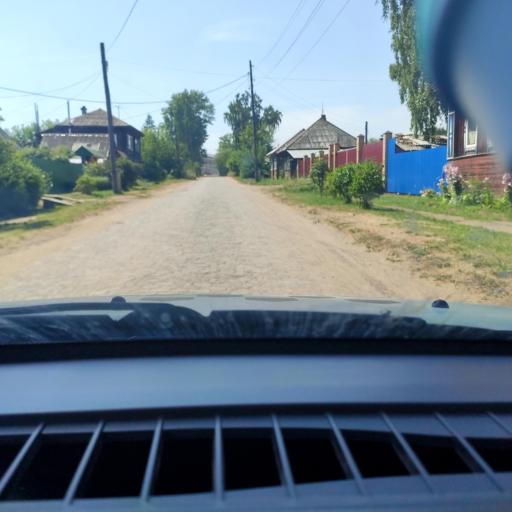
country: RU
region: Perm
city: Okhansk
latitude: 57.7238
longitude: 55.3961
